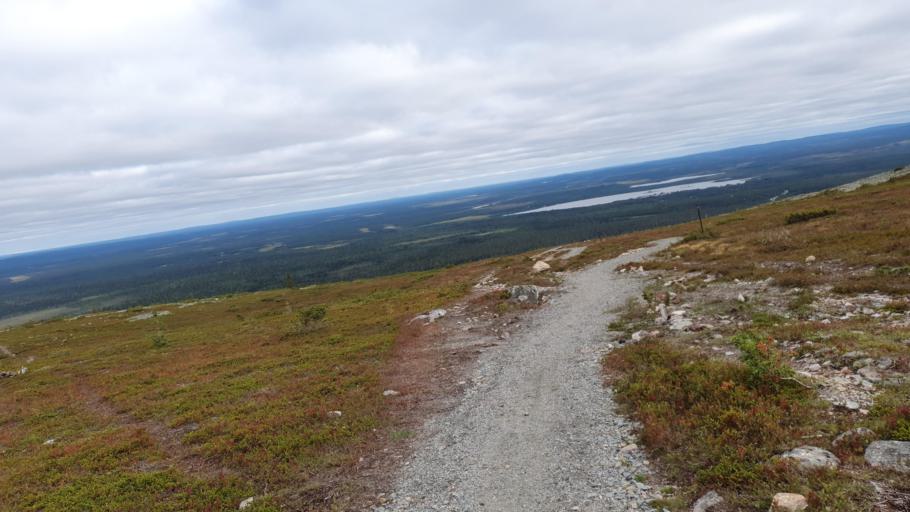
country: FI
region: Lapland
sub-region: Tunturi-Lappi
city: Kolari
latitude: 67.5667
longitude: 24.2484
